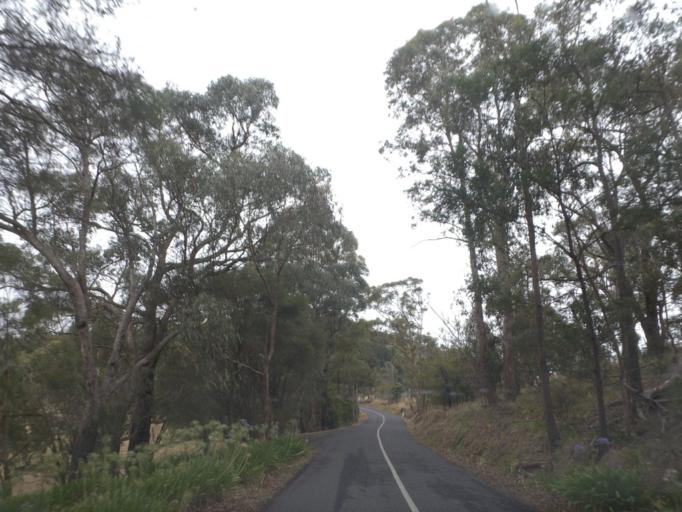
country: AU
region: Victoria
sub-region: Nillumbik
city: Saint Andrews
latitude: -37.6066
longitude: 145.3028
